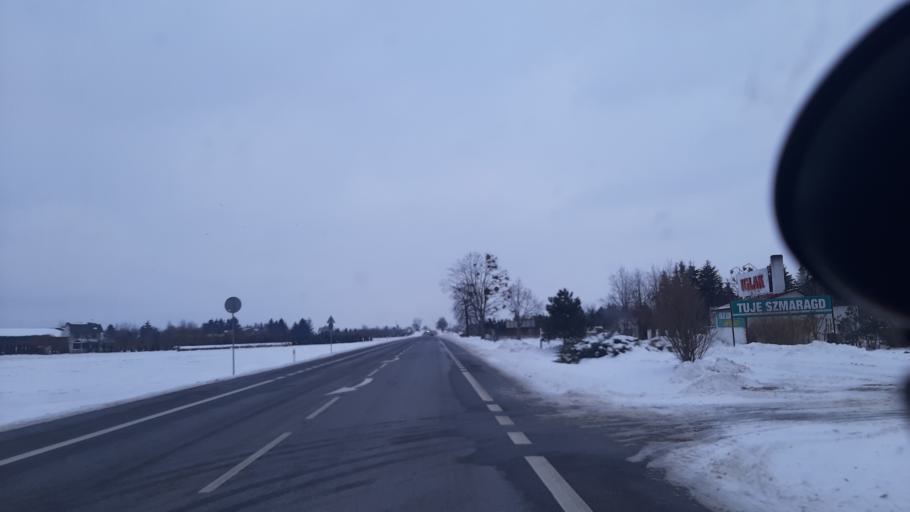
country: PL
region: Lublin Voivodeship
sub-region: Powiat pulawski
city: Kurow
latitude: 51.3846
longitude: 22.2149
